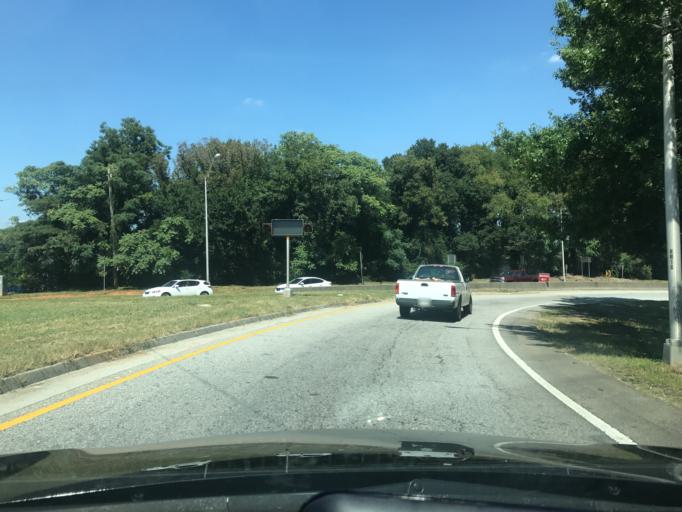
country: US
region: Georgia
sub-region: DeKalb County
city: Druid Hills
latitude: 33.7464
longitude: -84.3490
